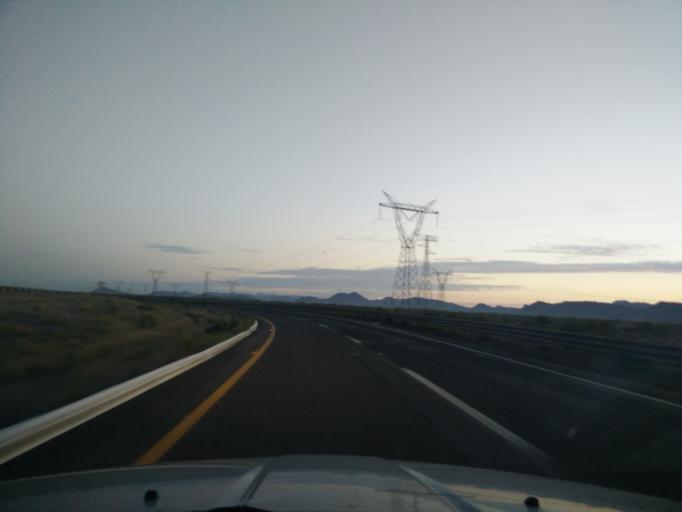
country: MX
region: Sonora
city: Heroica Guaymas
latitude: 28.0957
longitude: -110.9586
